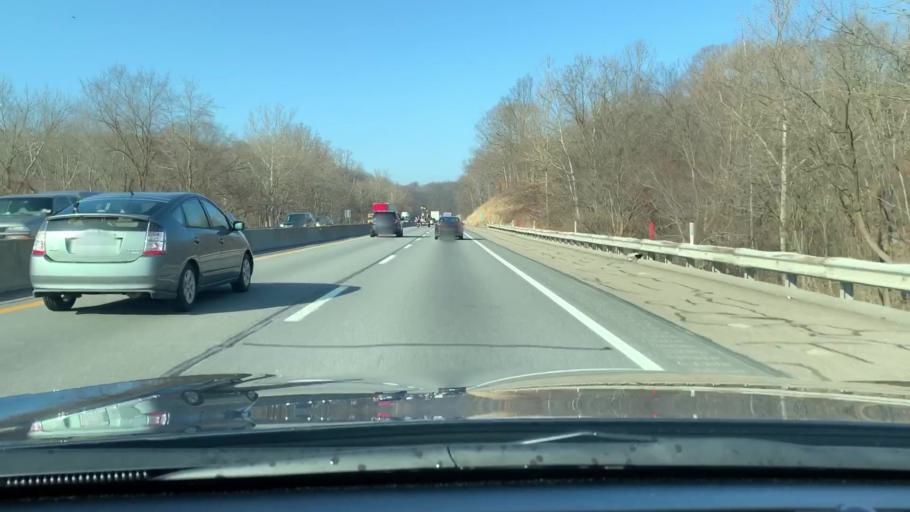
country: US
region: Pennsylvania
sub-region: Chester County
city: Downingtown
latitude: 40.0906
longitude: -75.7291
